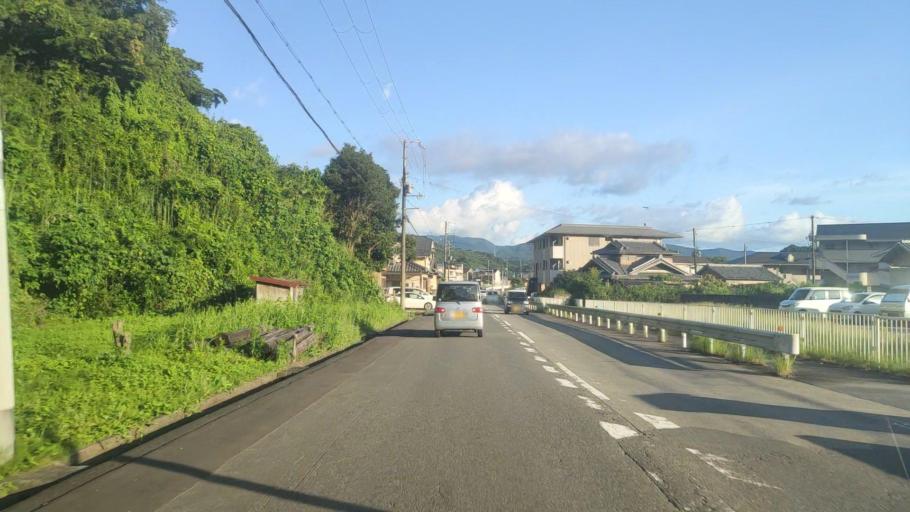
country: JP
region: Wakayama
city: Tanabe
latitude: 33.7234
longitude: 135.4450
